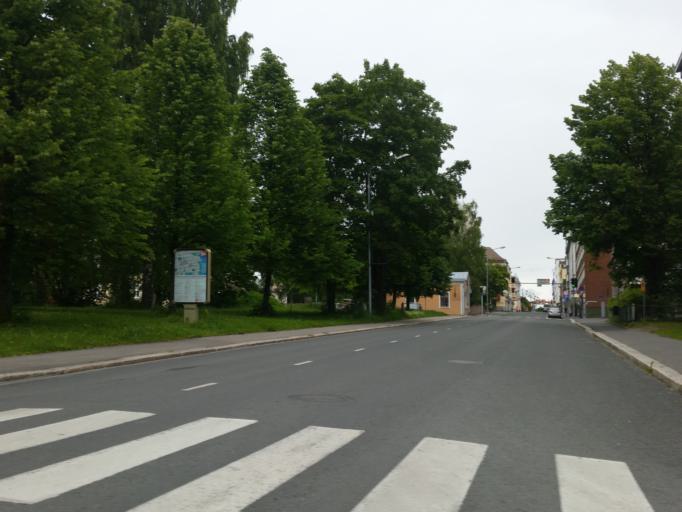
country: FI
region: Northern Savo
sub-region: Kuopio
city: Kuopio
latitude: 62.8889
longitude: 27.6807
